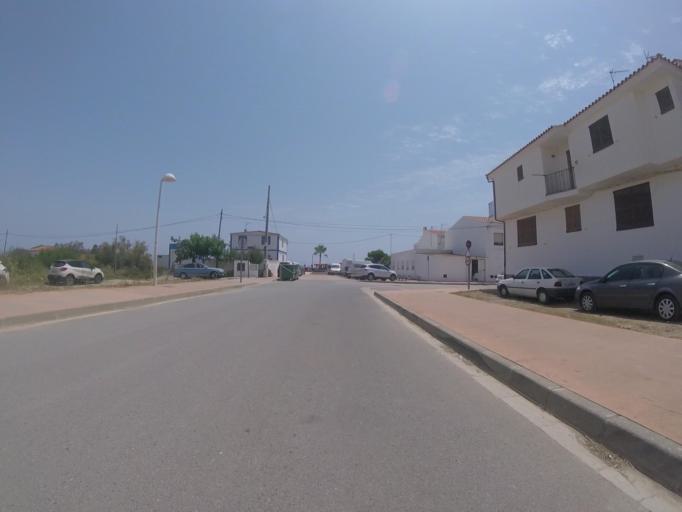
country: ES
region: Valencia
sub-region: Provincia de Castello
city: Orpesa/Oropesa del Mar
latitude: 40.1354
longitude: 0.1658
